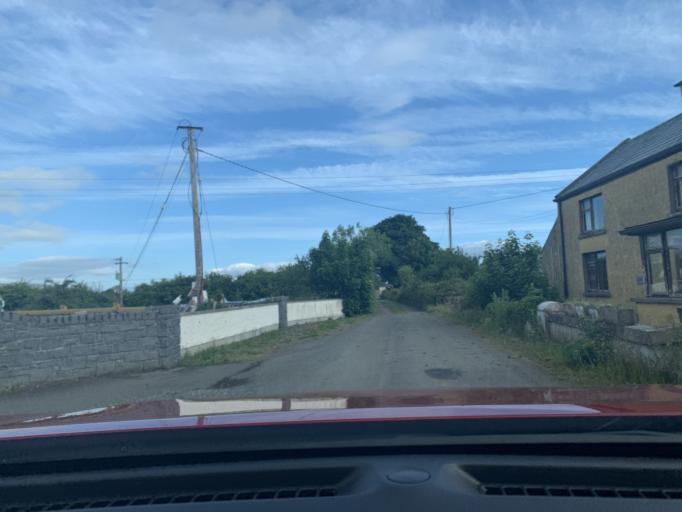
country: IE
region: Connaught
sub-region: Sligo
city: Sligo
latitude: 54.2347
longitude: -8.4680
